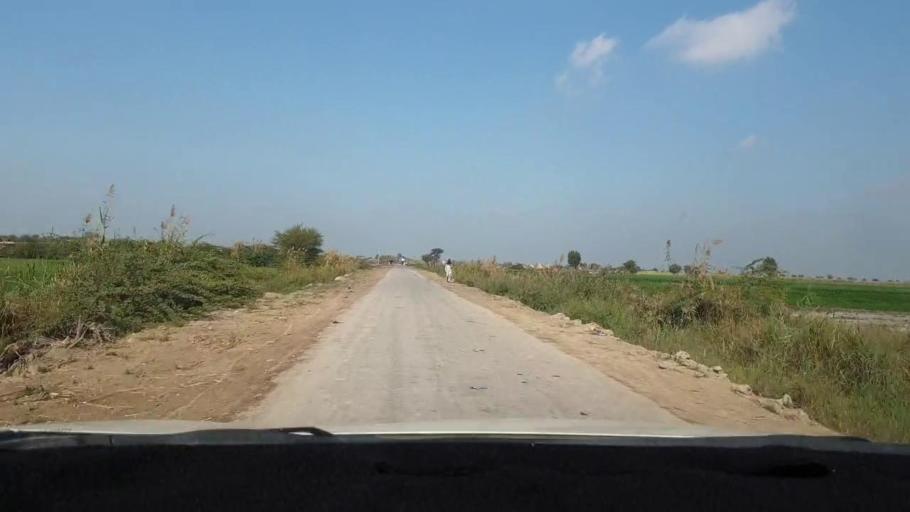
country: PK
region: Sindh
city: Berani
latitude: 25.7960
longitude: 68.8367
